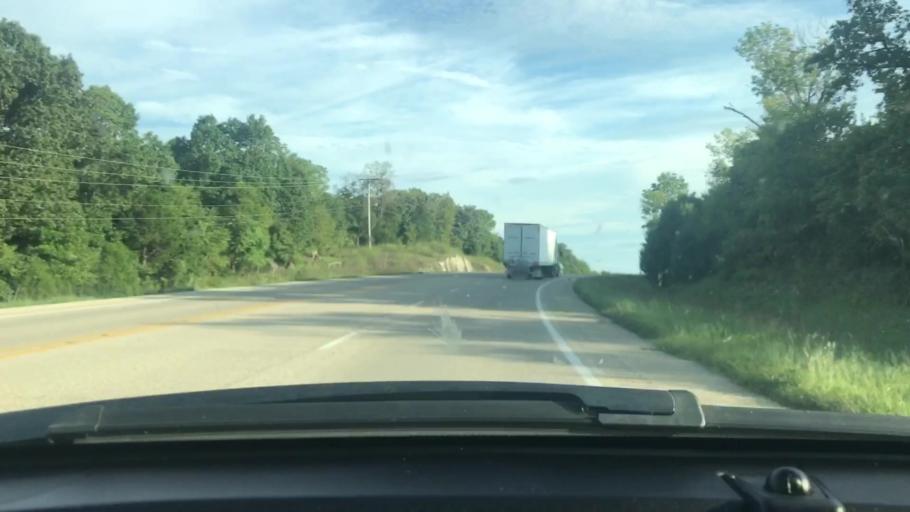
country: US
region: Arkansas
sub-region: Randolph County
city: Pocahontas
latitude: 36.1880
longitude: -91.1631
